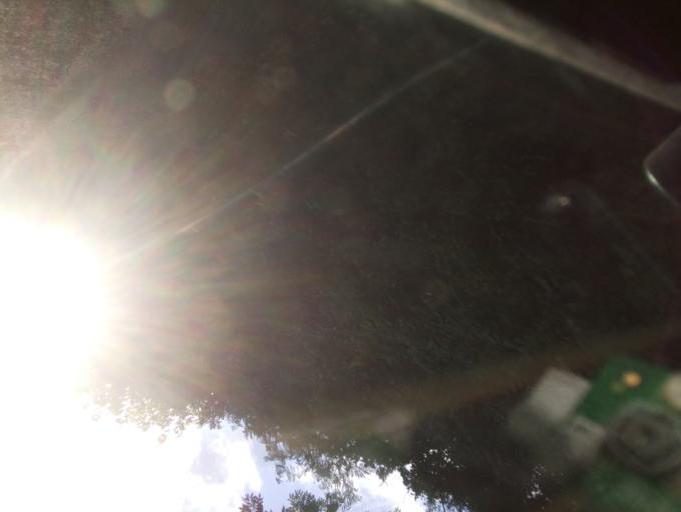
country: GB
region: England
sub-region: Devon
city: Dartmouth
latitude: 50.3468
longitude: -3.6467
